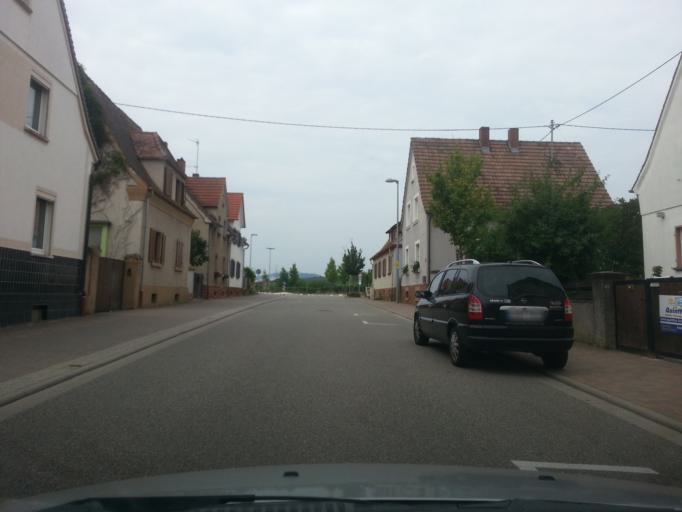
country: DE
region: Rheinland-Pfalz
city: Siebeldingen
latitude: 49.2118
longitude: 8.0689
